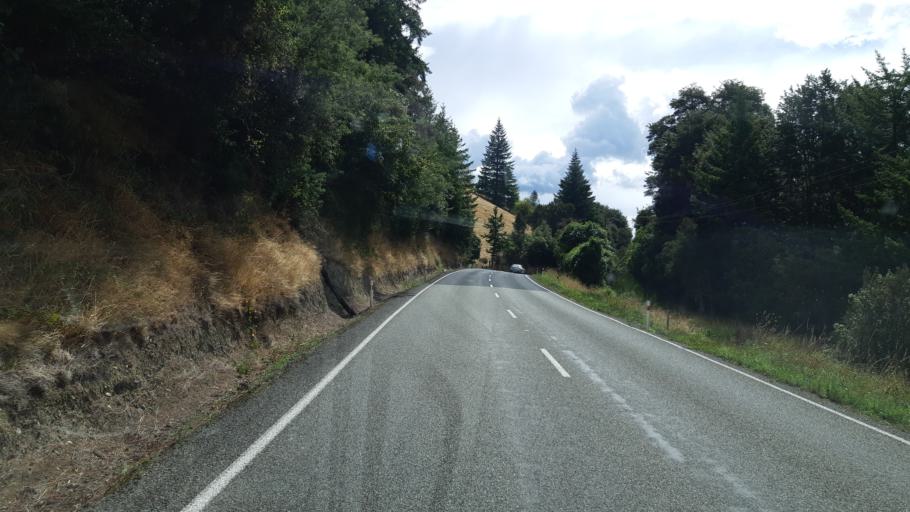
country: NZ
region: Tasman
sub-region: Tasman District
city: Wakefield
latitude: -41.5015
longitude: 172.7950
